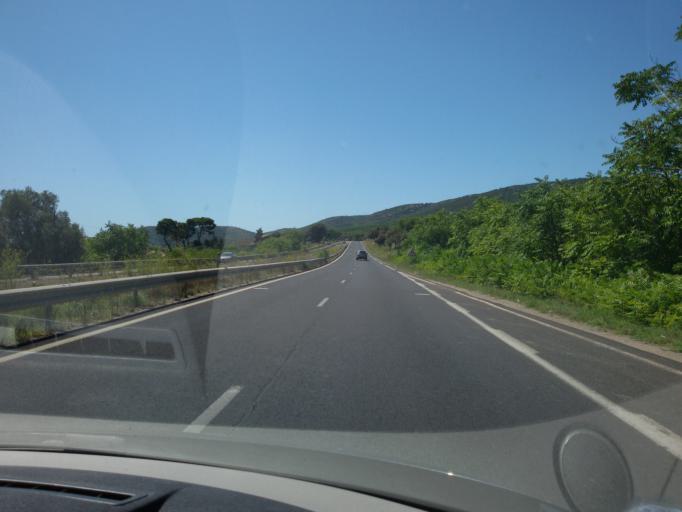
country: FR
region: Languedoc-Roussillon
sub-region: Departement de l'Herault
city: Vic-la-Gardiole
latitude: 43.5000
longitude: 3.7841
